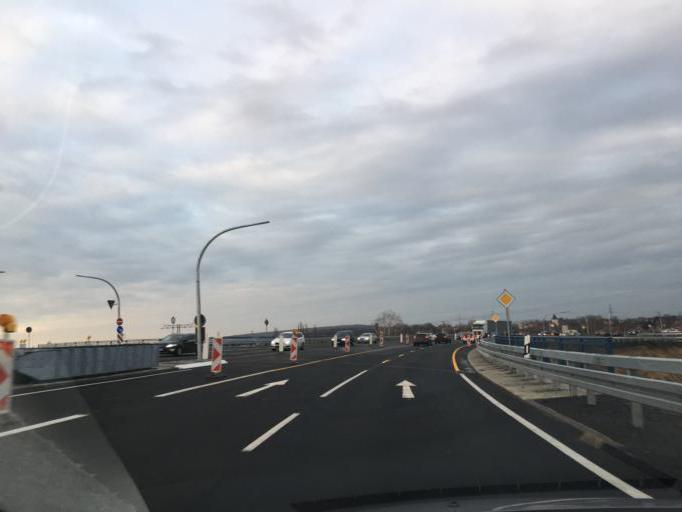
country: DE
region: Saxony
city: Borna
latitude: 51.1417
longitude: 12.5056
